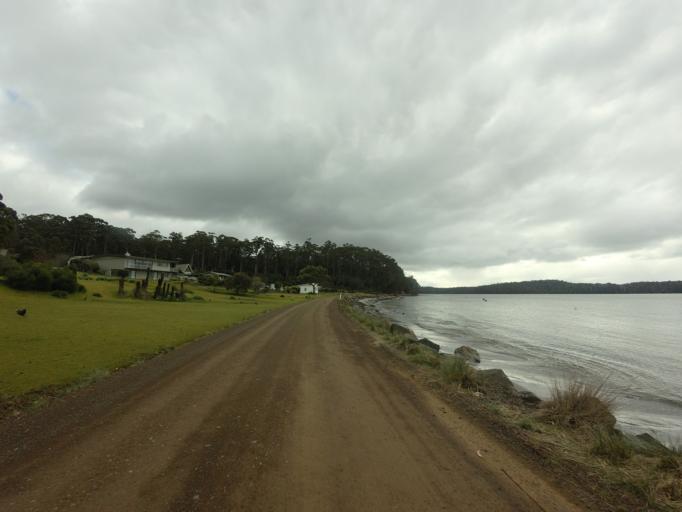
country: AU
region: Tasmania
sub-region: Huon Valley
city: Geeveston
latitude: -43.5348
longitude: 146.8906
